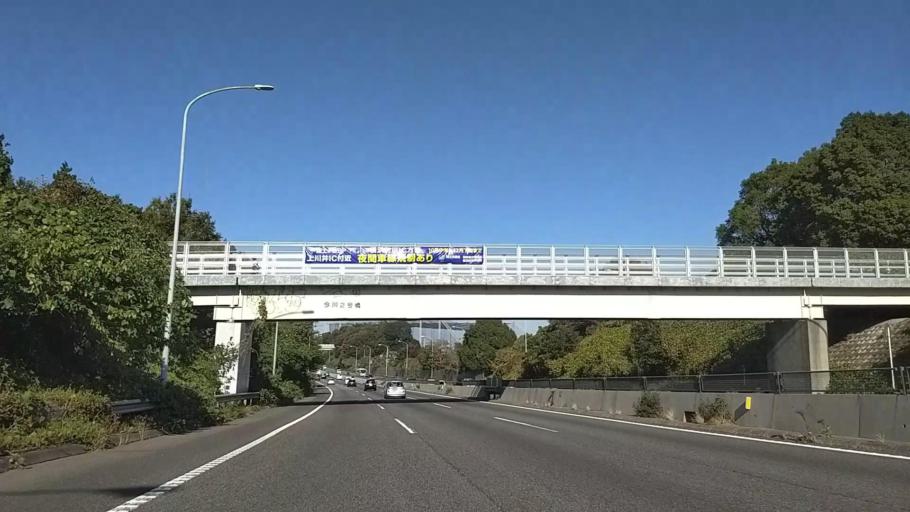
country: JP
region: Kanagawa
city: Minami-rinkan
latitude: 35.4742
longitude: 139.5295
